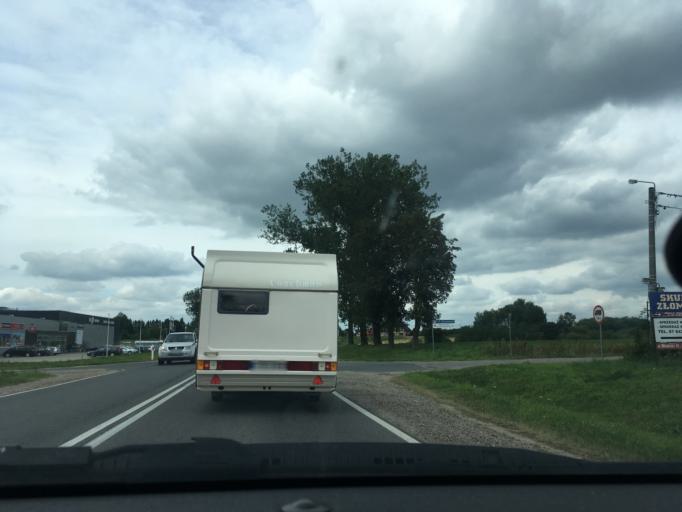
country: PL
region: Podlasie
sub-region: Powiat augustowski
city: Augustow
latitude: 53.8419
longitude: 22.9608
